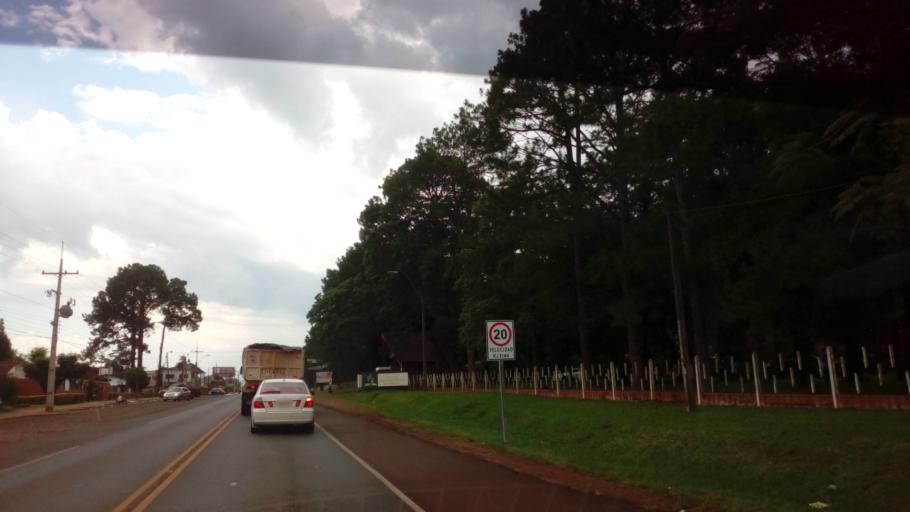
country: PY
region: Itapua
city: Obligado
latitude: -27.0751
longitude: -55.6416
